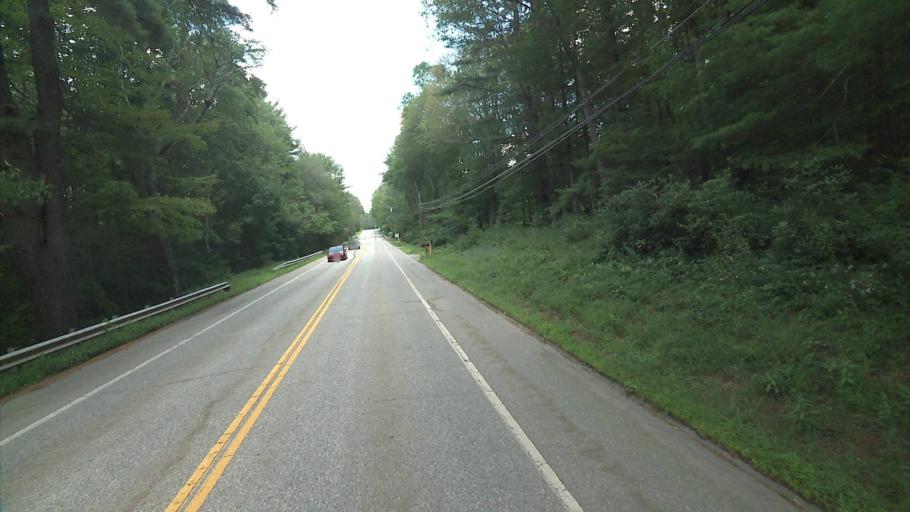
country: US
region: Connecticut
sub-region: Tolland County
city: Storrs
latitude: 41.8589
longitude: -72.1624
